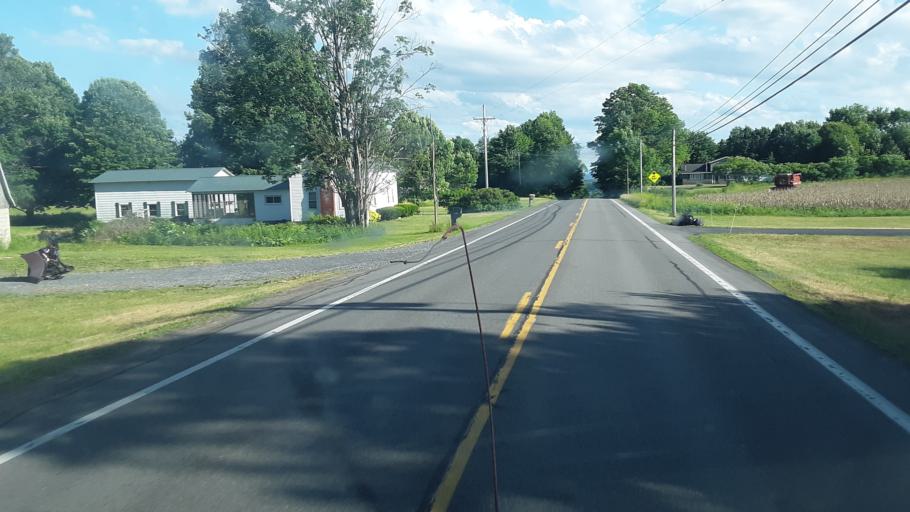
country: US
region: New York
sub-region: Oneida County
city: Rome
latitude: 43.3137
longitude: -75.4749
